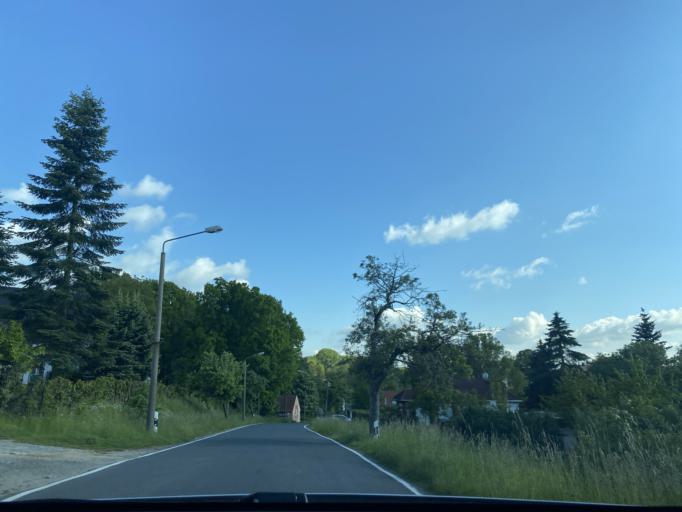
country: DE
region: Saxony
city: Markersdorf
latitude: 51.1435
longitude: 14.9241
